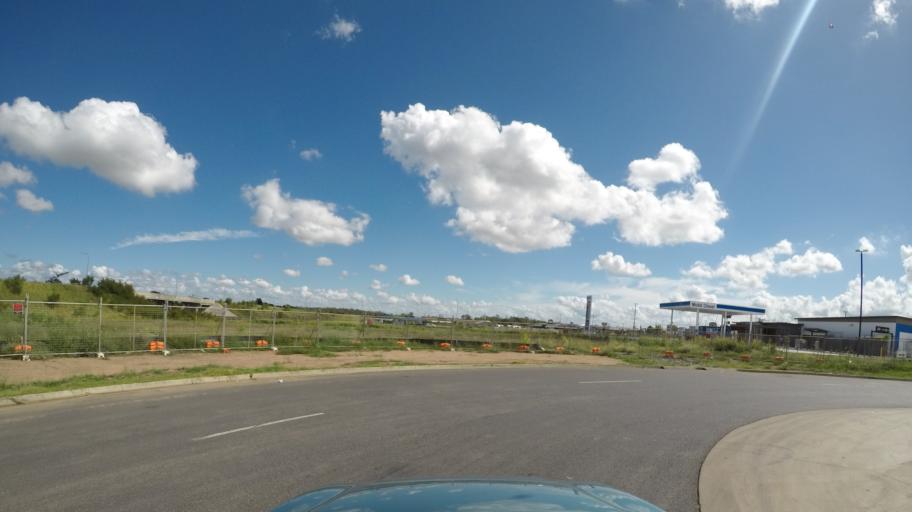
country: AU
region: Queensland
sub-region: Lockyer Valley
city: Gatton
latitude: -27.5665
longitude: 152.4215
